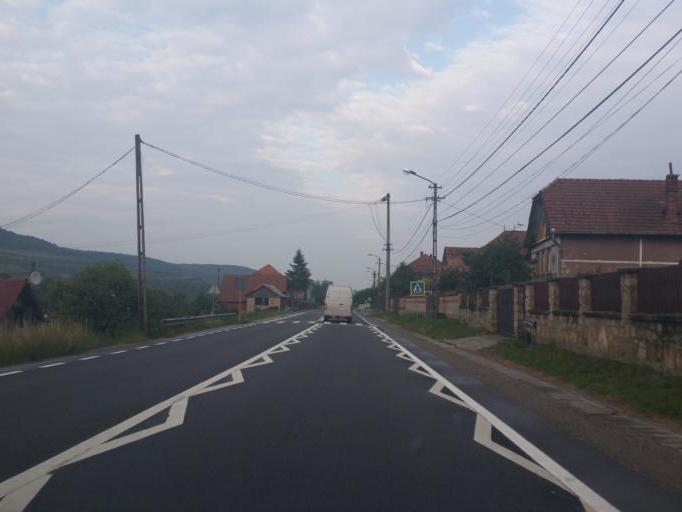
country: RO
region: Cluj
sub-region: Comuna Baciu
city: Mera
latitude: 46.8008
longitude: 23.4618
